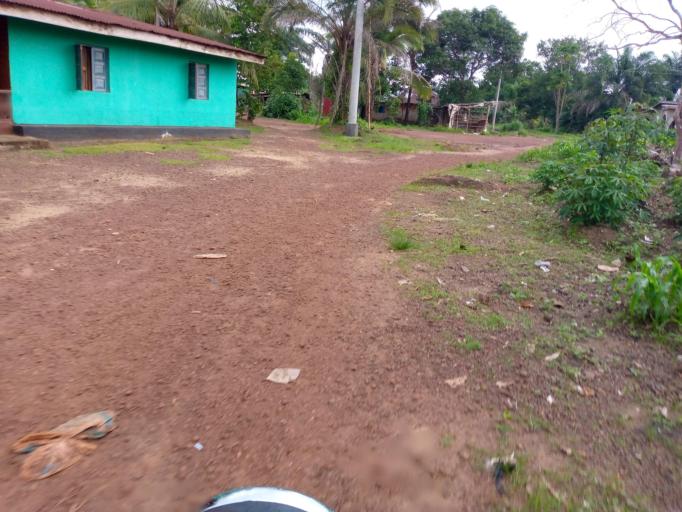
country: SL
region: Southern Province
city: Moyamba
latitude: 8.1520
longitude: -12.4341
